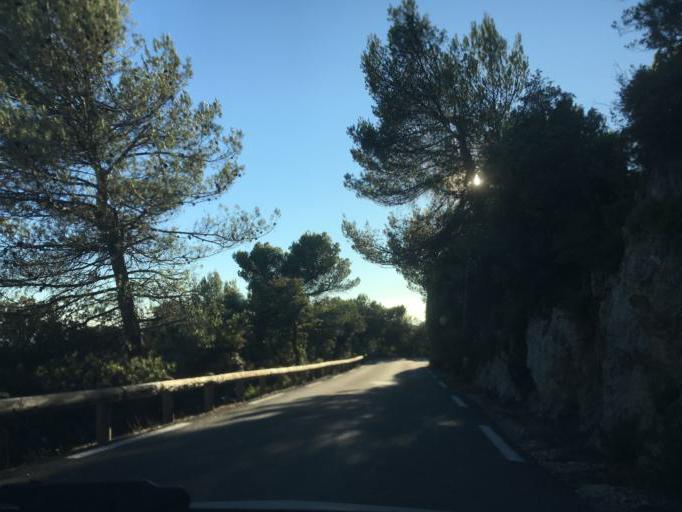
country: FR
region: Provence-Alpes-Cote d'Azur
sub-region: Departement du Var
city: Villecroze
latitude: 43.5959
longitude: 6.3291
